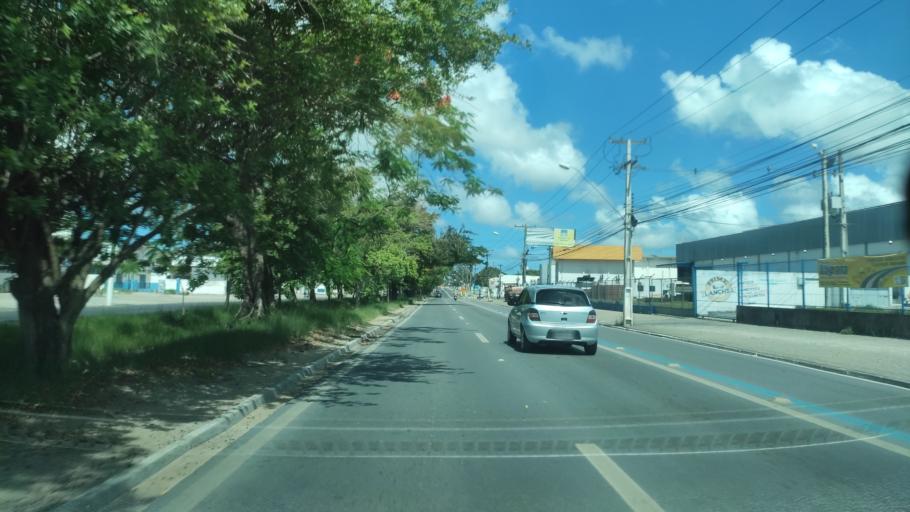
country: BR
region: Alagoas
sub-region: Satuba
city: Satuba
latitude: -9.5791
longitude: -35.7686
